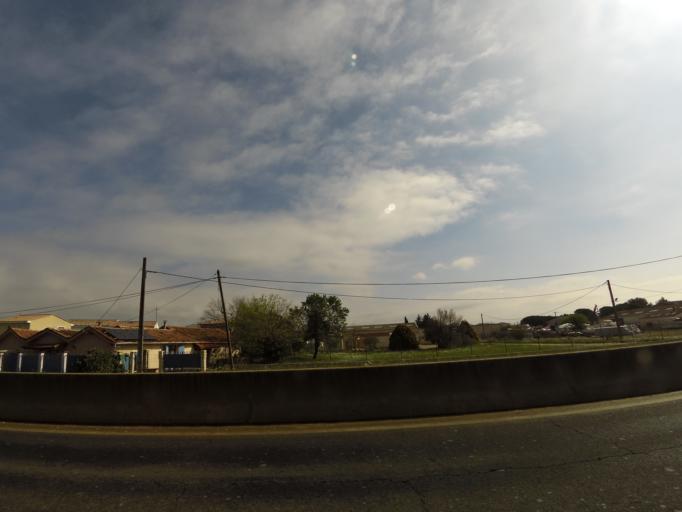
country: FR
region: Languedoc-Roussillon
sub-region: Departement du Gard
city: Aimargues
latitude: 43.6998
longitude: 4.1959
